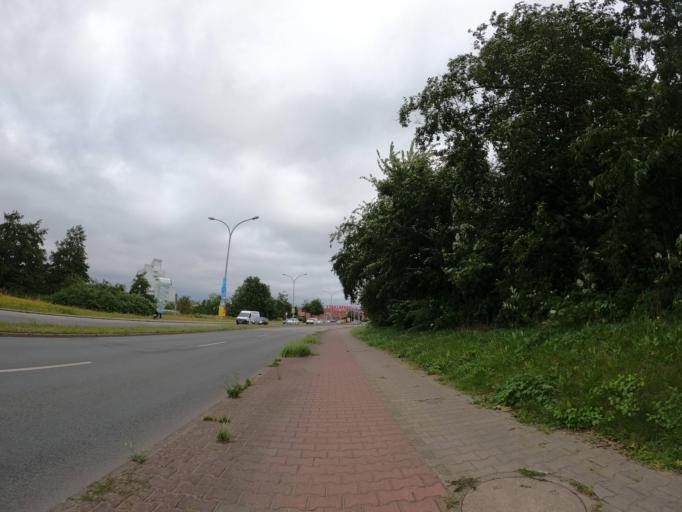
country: DE
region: Mecklenburg-Vorpommern
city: Kramerhof
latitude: 54.3176
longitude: 13.0454
